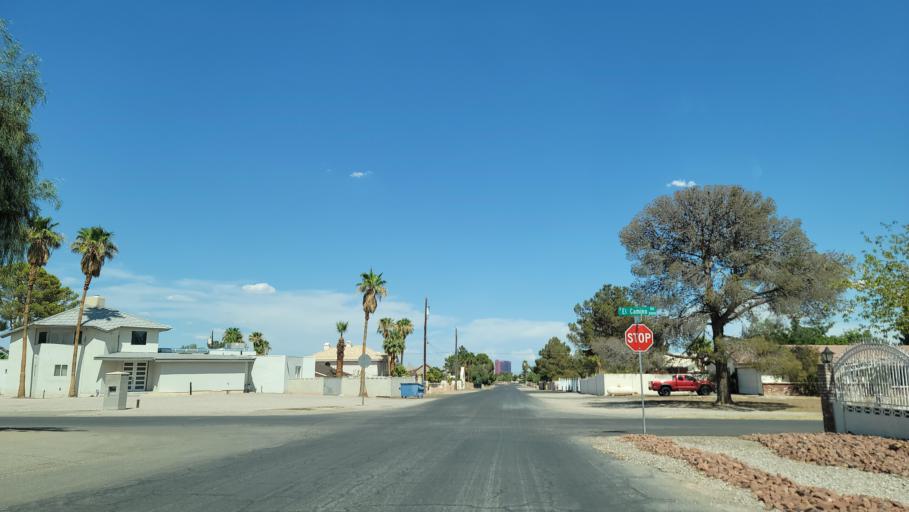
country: US
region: Nevada
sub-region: Clark County
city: Spring Valley
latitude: 36.1348
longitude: -115.2299
